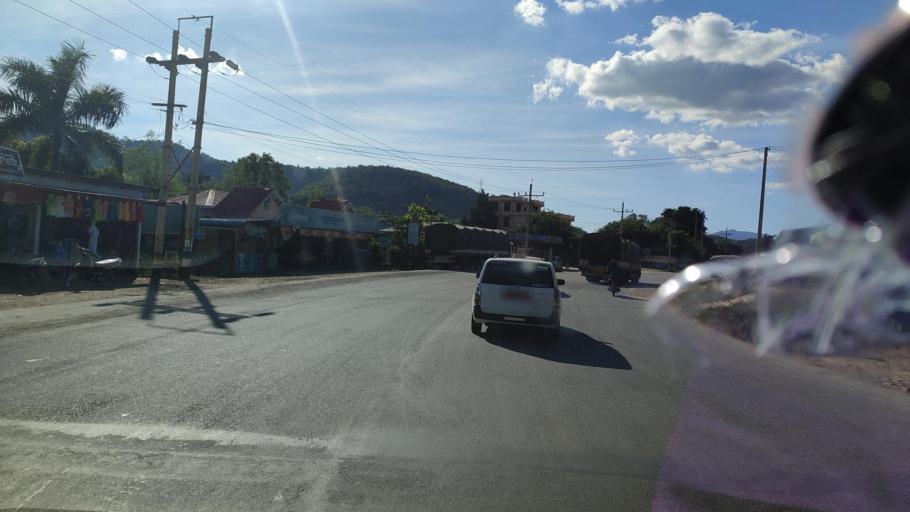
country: MM
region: Mandalay
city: Yamethin
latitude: 20.8173
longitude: 96.3940
